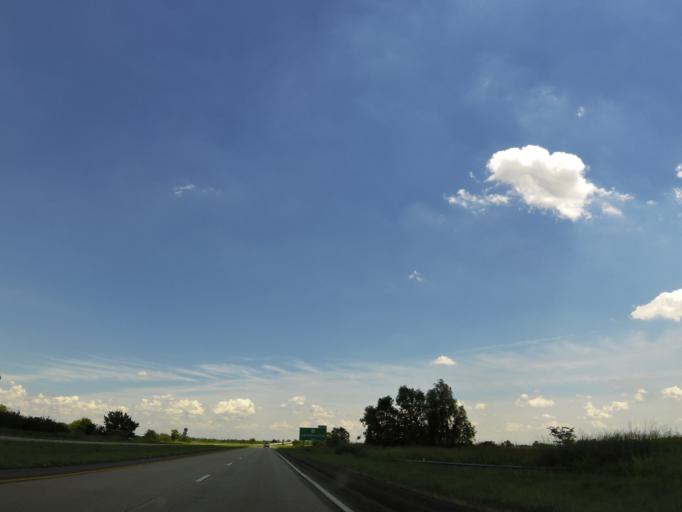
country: US
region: Missouri
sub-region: Pemiscot County
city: Caruthersville
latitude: 36.1895
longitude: -89.7099
